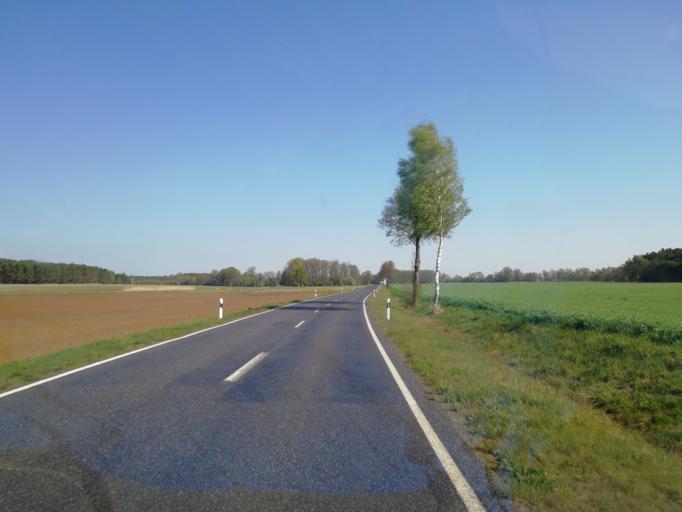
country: DE
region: Brandenburg
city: Crinitz
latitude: 51.7480
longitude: 13.8558
